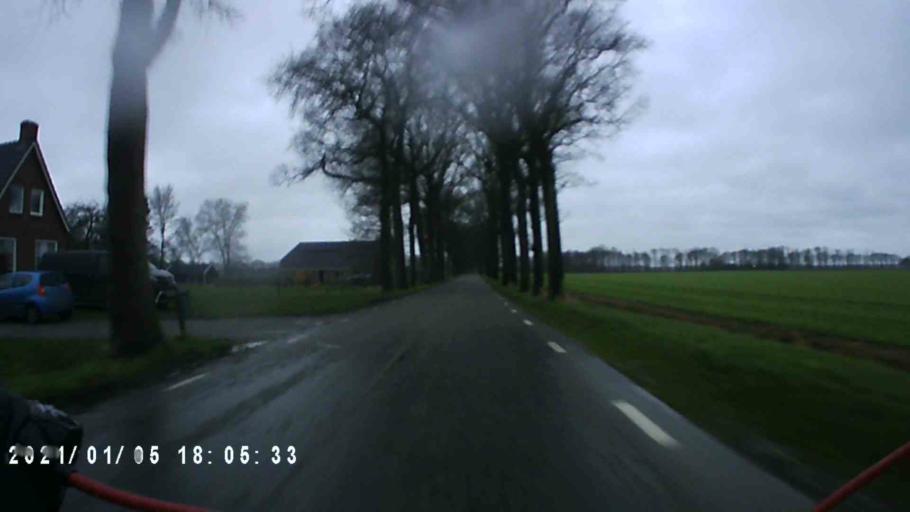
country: NL
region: Groningen
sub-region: Gemeente Slochteren
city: Slochteren
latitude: 53.1999
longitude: 6.8476
